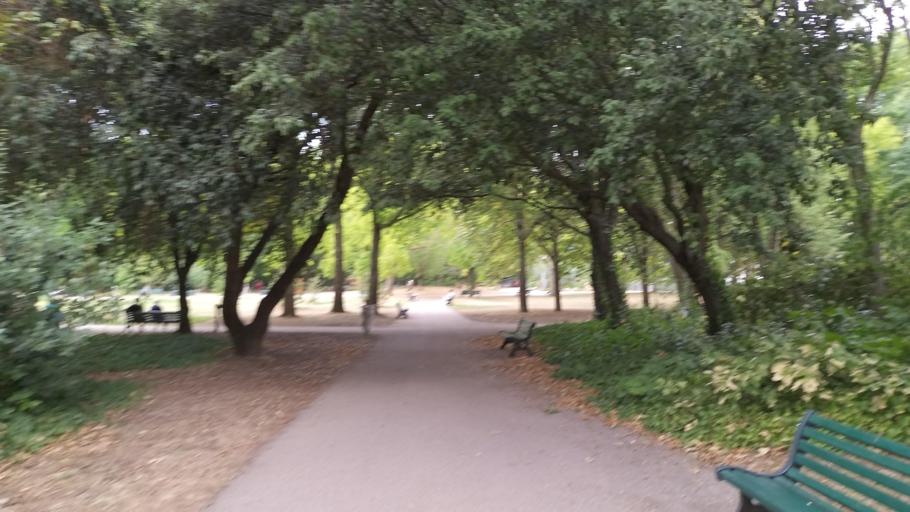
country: FR
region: Midi-Pyrenees
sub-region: Departement de la Haute-Garonne
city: Toulouse
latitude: 43.6102
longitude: 1.4331
